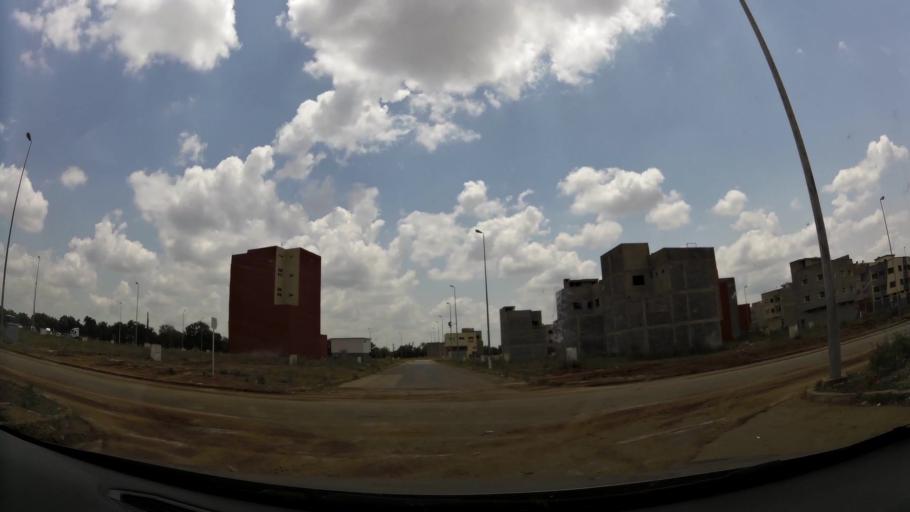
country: MA
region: Rabat-Sale-Zemmour-Zaer
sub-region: Khemisset
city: Tiflet
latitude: 33.9995
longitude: -6.5220
